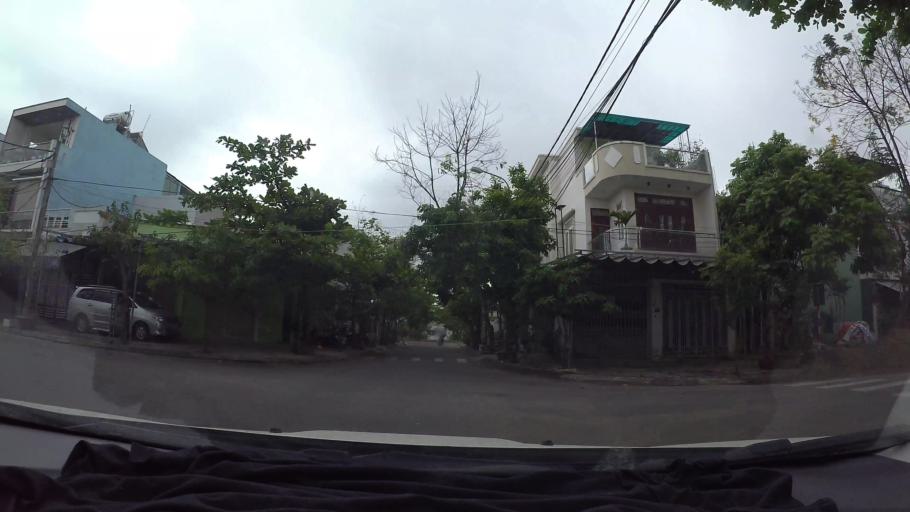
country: VN
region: Da Nang
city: Lien Chieu
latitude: 16.0524
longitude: 108.1672
